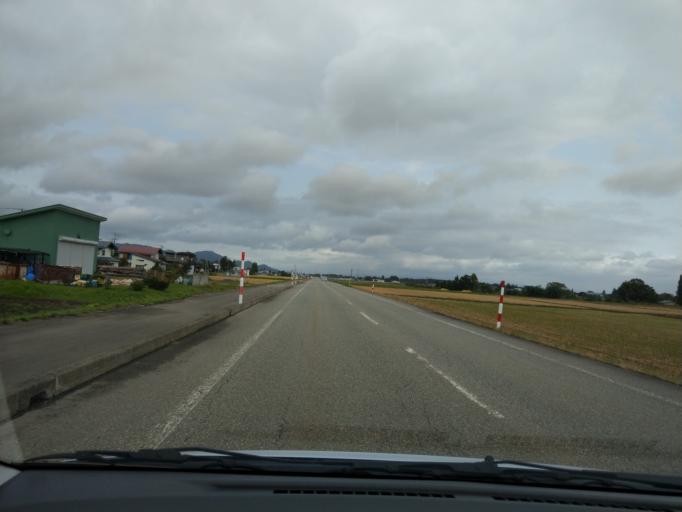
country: JP
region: Akita
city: Omagari
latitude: 39.3860
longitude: 140.4860
